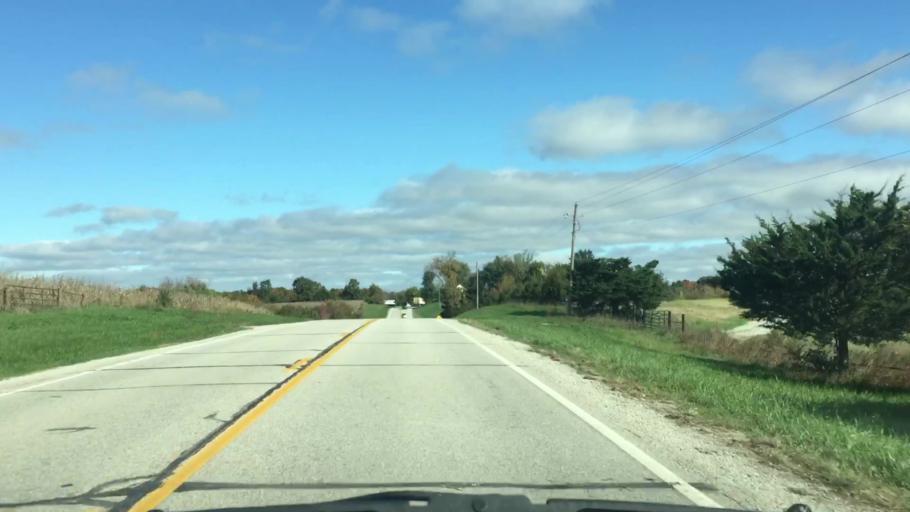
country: US
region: Iowa
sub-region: Decatur County
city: Leon
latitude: 40.6931
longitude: -93.7747
